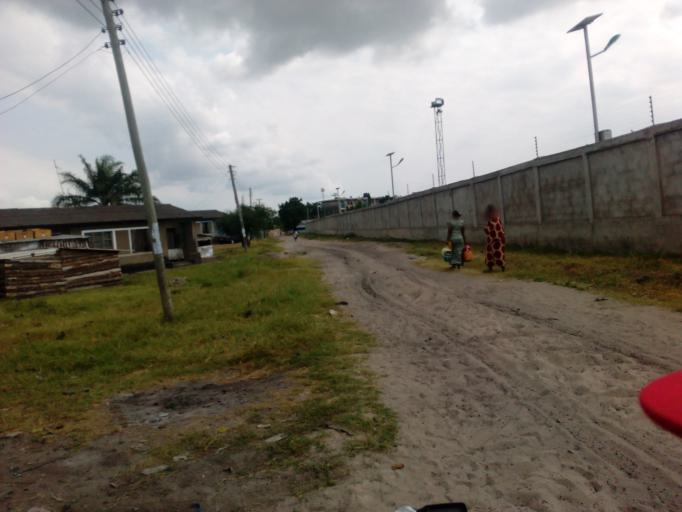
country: TZ
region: Dar es Salaam
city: Dar es Salaam
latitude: -6.8494
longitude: 39.2573
